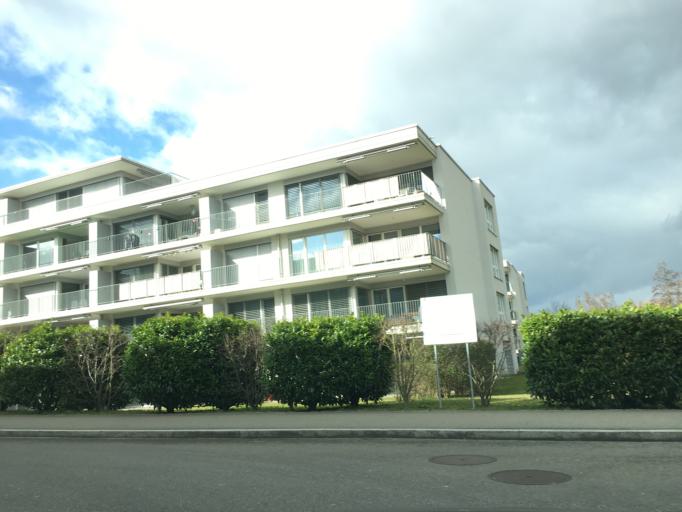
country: CH
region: Zurich
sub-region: Bezirk Buelach
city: Buelach / Seematt
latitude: 47.5109
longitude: 8.5408
